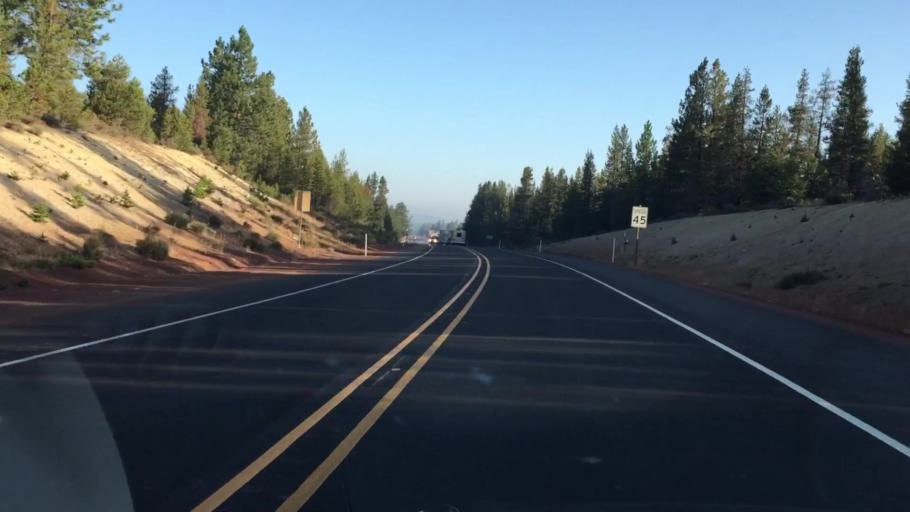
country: US
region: Oregon
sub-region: Deschutes County
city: La Pine
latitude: 43.2081
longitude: -121.7793
